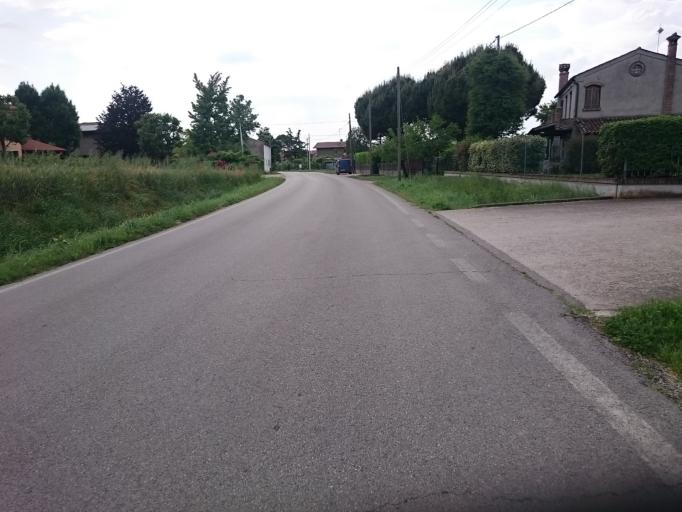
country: IT
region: Veneto
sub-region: Provincia di Padova
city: Santa Margherita d'Adige
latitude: 45.1969
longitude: 11.5646
